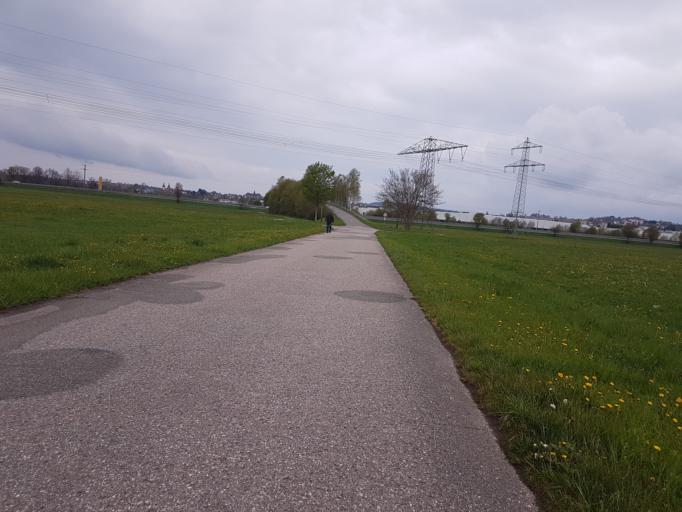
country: DE
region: Baden-Wuerttemberg
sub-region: Freiburg Region
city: Donaueschingen
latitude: 47.9628
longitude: 8.5191
